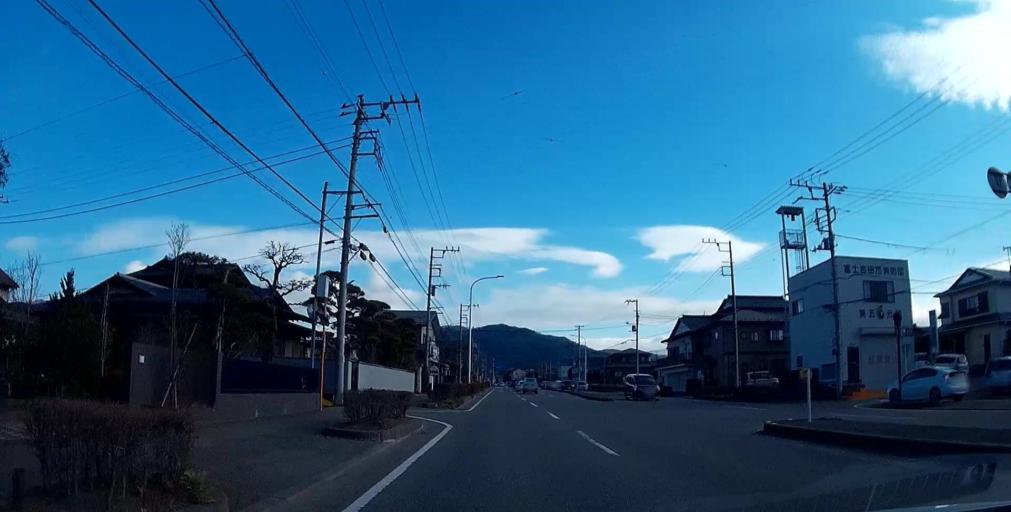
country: JP
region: Yamanashi
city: Fujikawaguchiko
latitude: 35.4879
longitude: 138.7979
